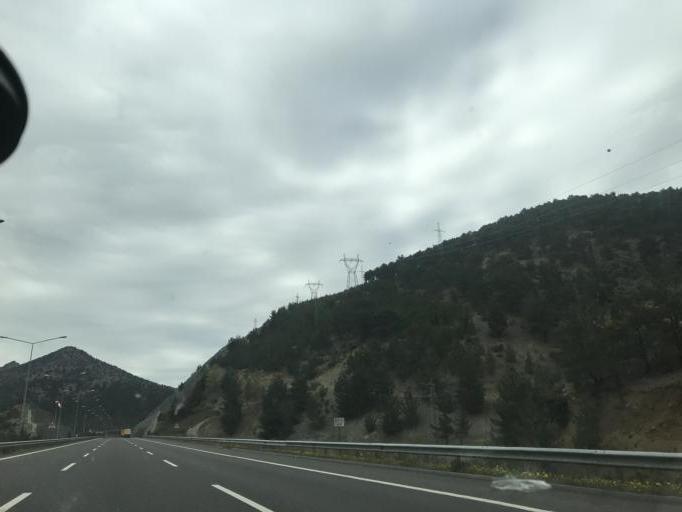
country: TR
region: Nigde
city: Ciftehan
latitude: 37.4983
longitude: 34.8281
